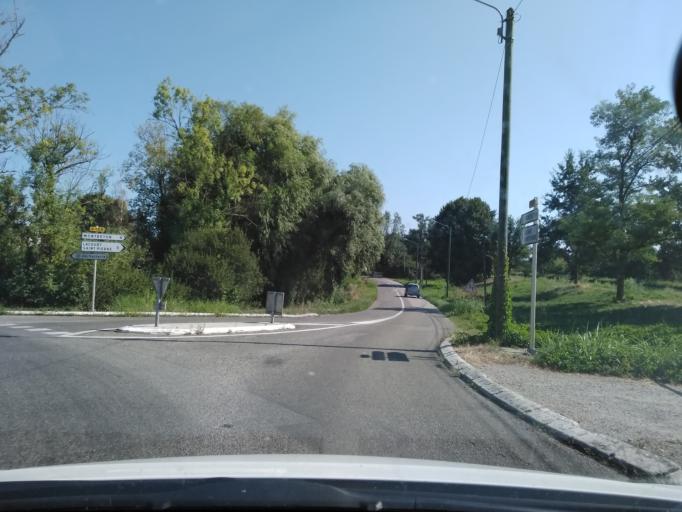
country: FR
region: Midi-Pyrenees
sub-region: Departement du Tarn-et-Garonne
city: Montech
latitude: 43.9636
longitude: 1.2361
